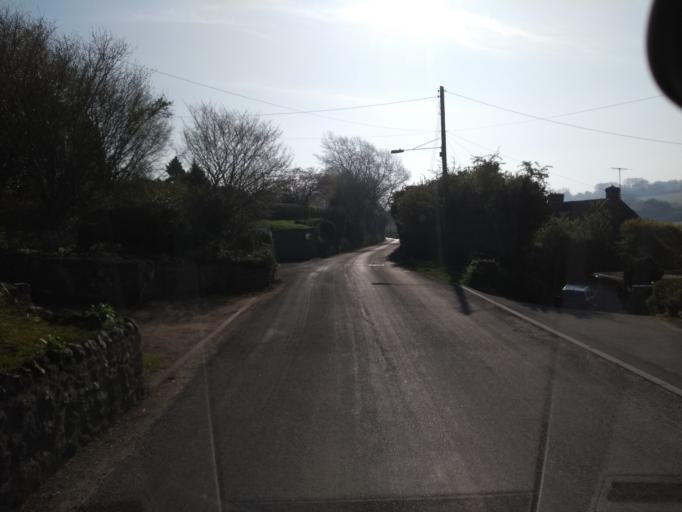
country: GB
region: England
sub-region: Somerset
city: Ilminster
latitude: 50.9265
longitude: -2.9008
